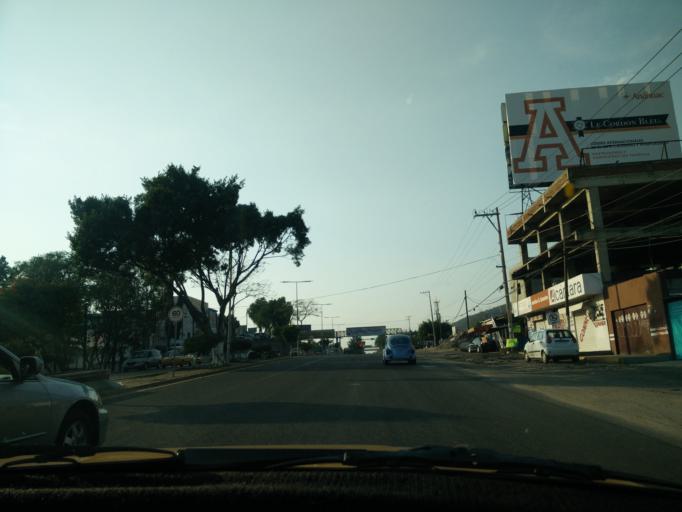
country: MX
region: Oaxaca
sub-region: Santa Maria Atzompa
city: San Jeronimo Yahuiche
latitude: 17.0919
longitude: -96.7476
